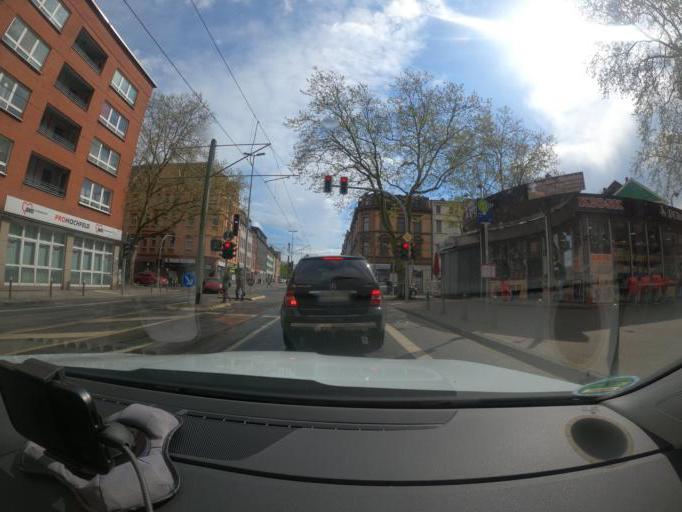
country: DE
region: North Rhine-Westphalia
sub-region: Regierungsbezirk Dusseldorf
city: Hochfeld
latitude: 51.4244
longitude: 6.7549
